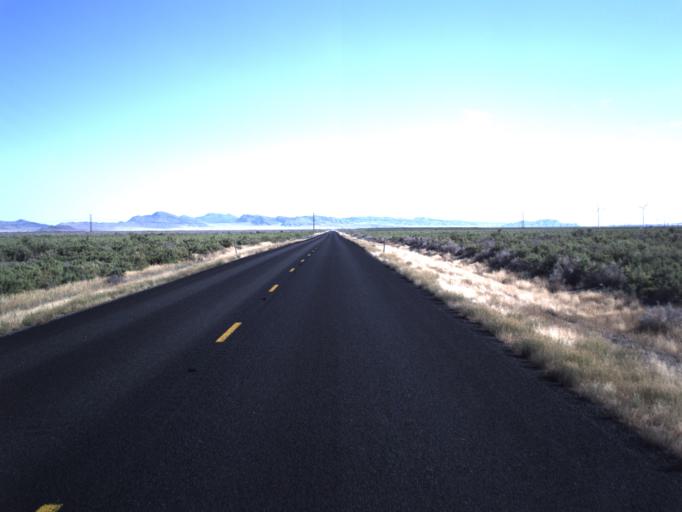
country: US
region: Utah
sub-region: Beaver County
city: Milford
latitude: 38.5595
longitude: -112.9910
